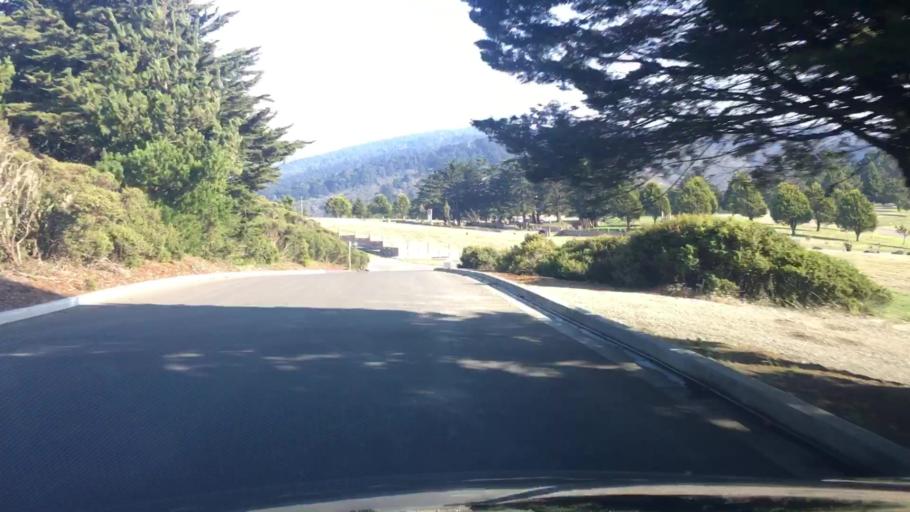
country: US
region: California
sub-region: San Mateo County
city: Highlands-Baywood Park
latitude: 37.5027
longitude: -122.3723
